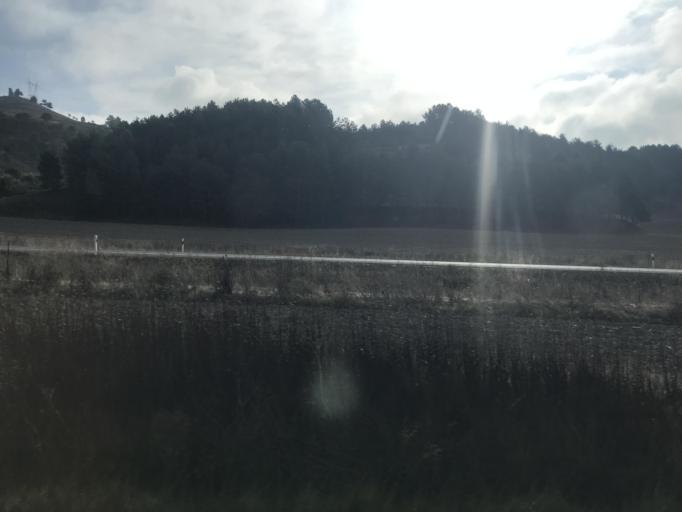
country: ES
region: Castille and Leon
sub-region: Provincia de Burgos
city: Pradanos de Bureba
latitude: 42.5129
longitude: -3.3402
